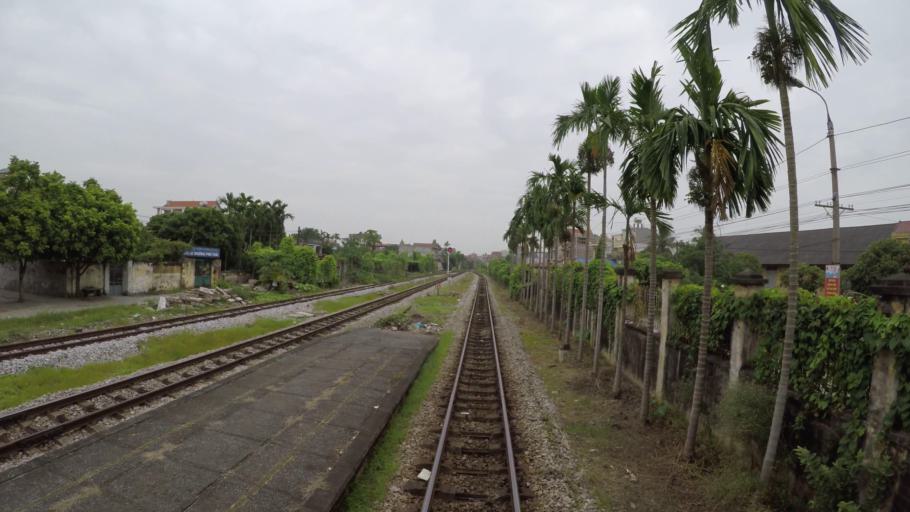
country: VN
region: Hai Duong
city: Phu Thai
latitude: 20.9728
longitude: 106.4885
